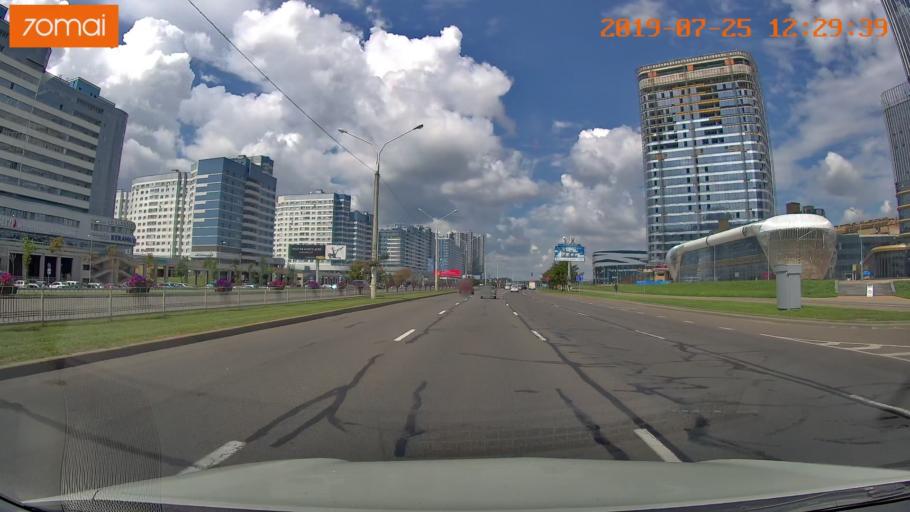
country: BY
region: Minsk
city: Zhdanovichy
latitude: 53.9395
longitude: 27.4722
